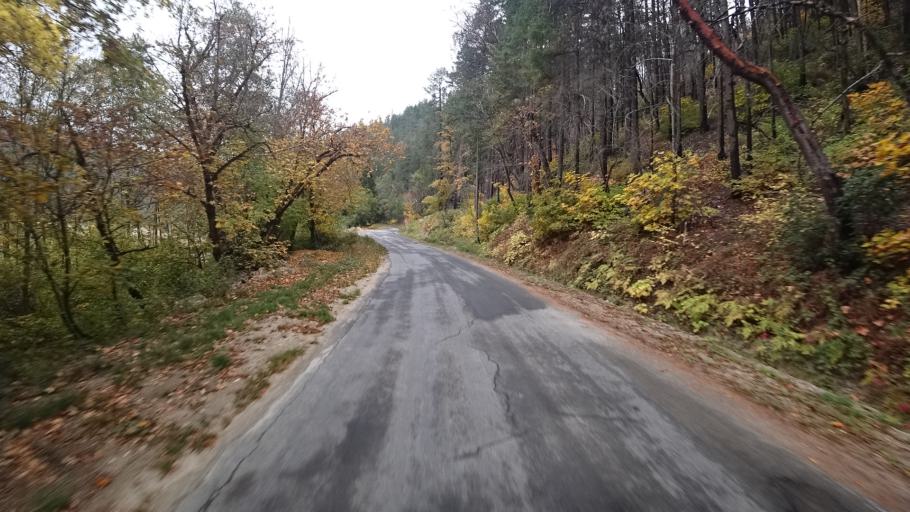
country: US
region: California
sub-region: Siskiyou County
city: Happy Camp
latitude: 41.8256
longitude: -123.1876
